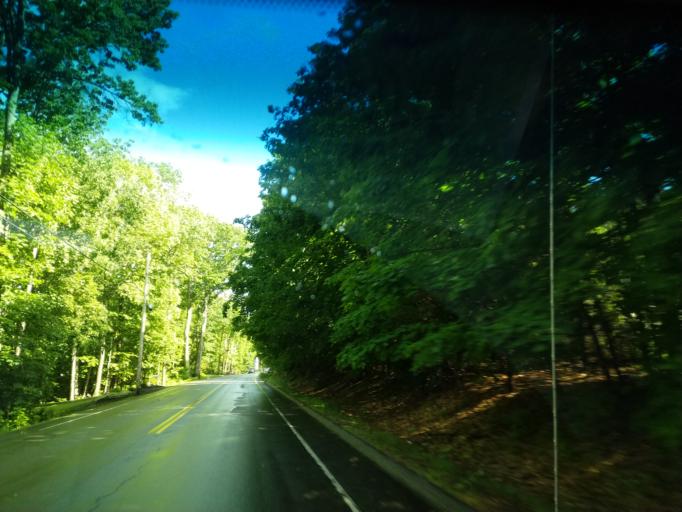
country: US
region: Maine
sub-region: Cumberland County
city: Cumberland Center
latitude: 43.7590
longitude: -70.3172
